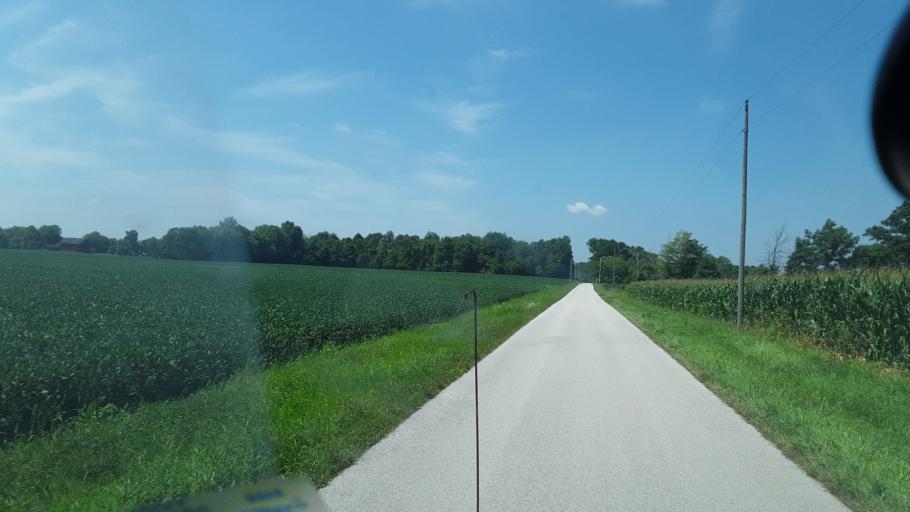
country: US
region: Ohio
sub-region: Hardin County
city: Forest
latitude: 40.8401
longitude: -83.5366
